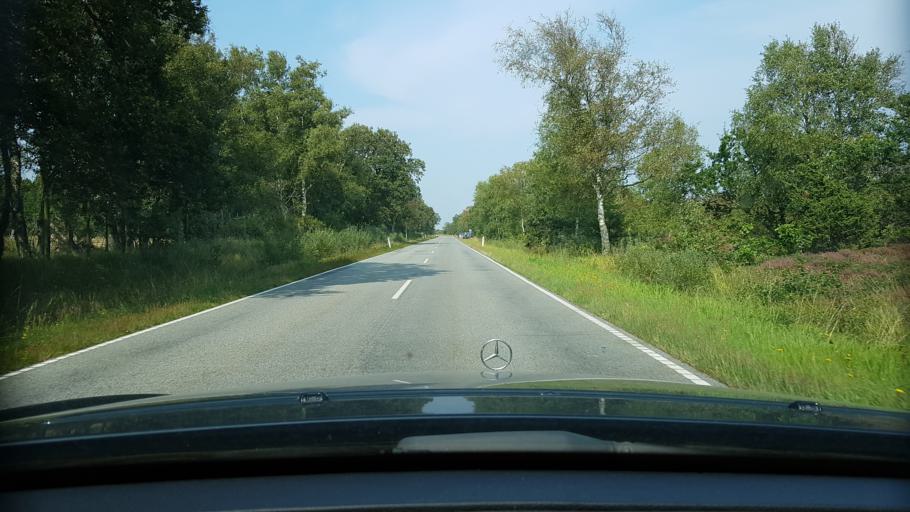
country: DK
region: North Denmark
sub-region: Alborg Kommune
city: Hals
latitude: 56.8428
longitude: 10.2672
